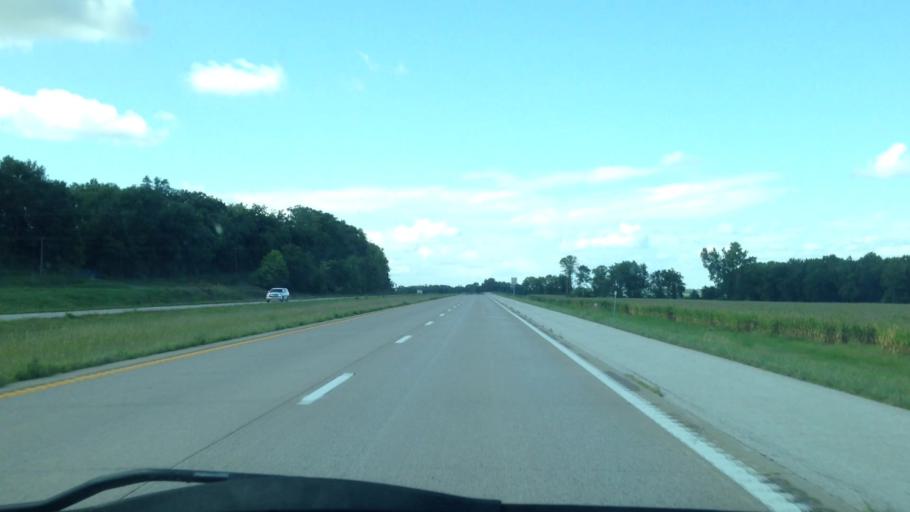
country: US
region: Missouri
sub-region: Lewis County
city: Canton
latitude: 40.2171
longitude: -91.5255
